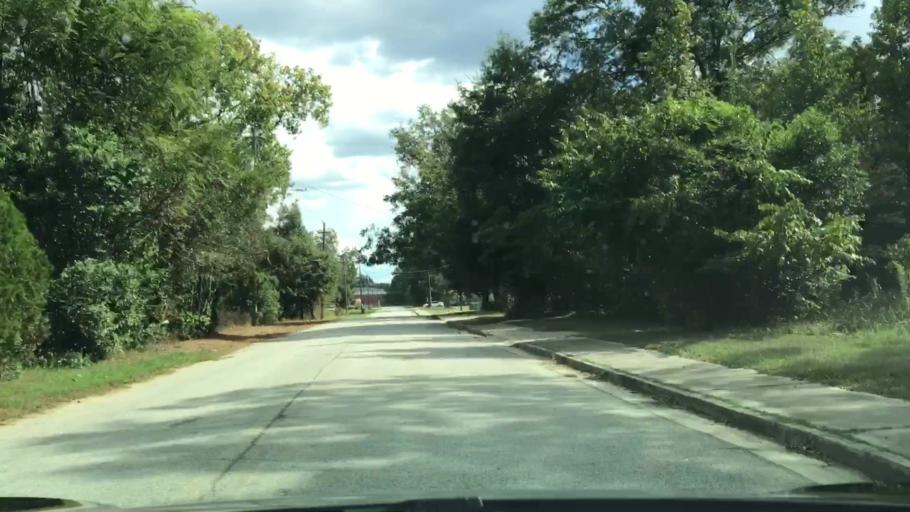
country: US
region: Georgia
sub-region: Jefferson County
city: Wadley
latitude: 32.8594
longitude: -82.3968
